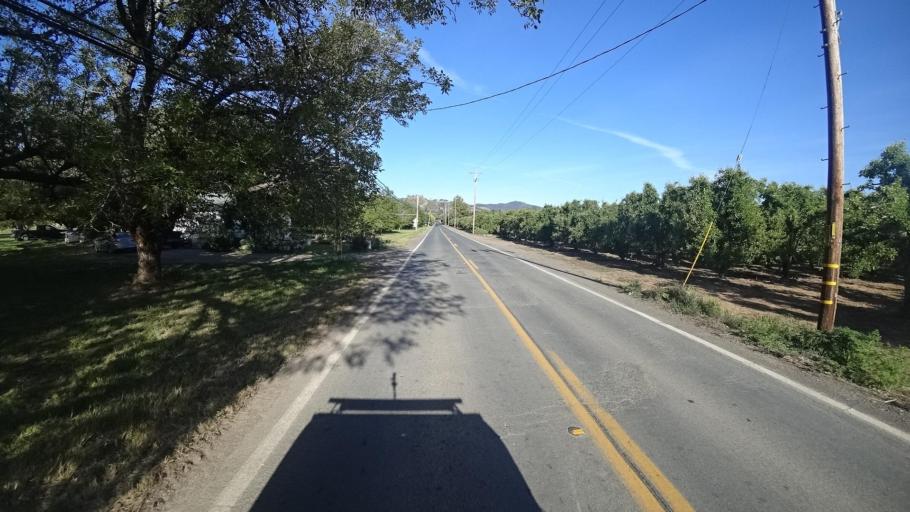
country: US
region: California
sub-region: Lake County
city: Lakeport
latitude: 39.0623
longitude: -122.9384
